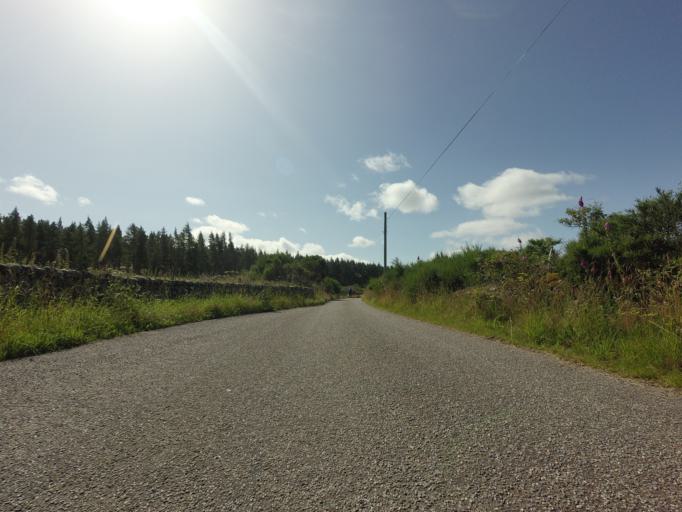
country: GB
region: Scotland
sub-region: Highland
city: Nairn
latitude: 57.5015
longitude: -3.9391
